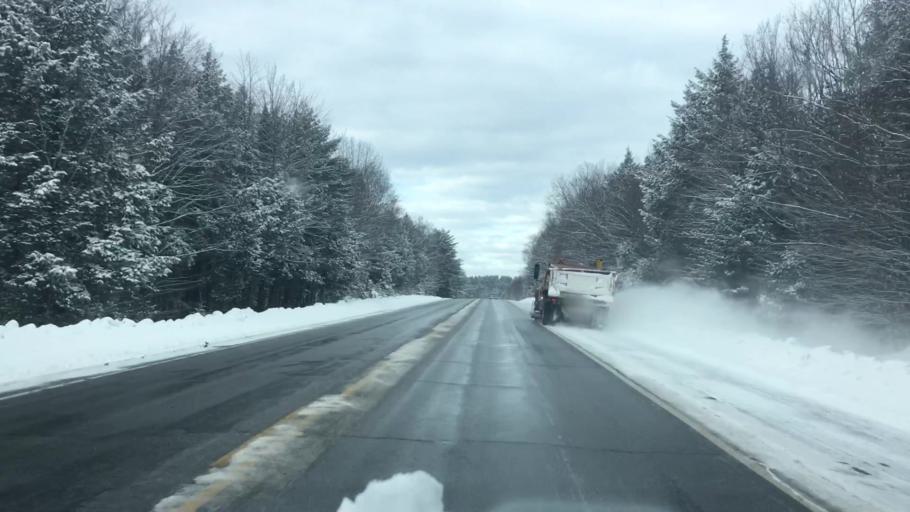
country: US
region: Maine
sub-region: Cumberland County
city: Bridgton
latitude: 44.0028
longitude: -70.6668
